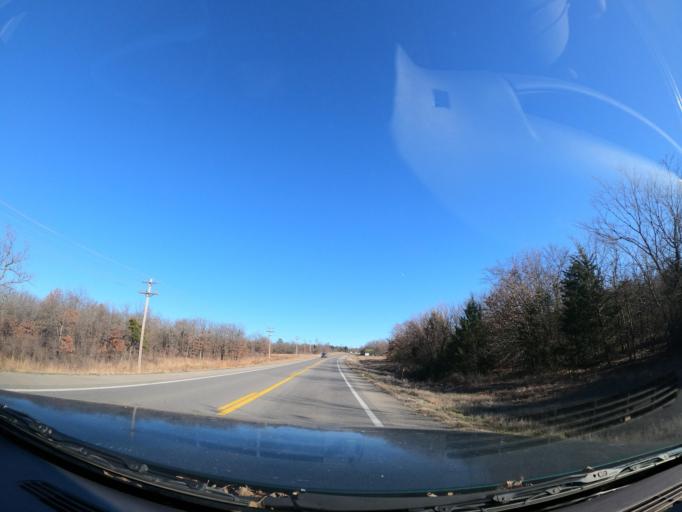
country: US
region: Oklahoma
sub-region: Pittsburg County
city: Longtown
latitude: 35.2391
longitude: -95.4755
